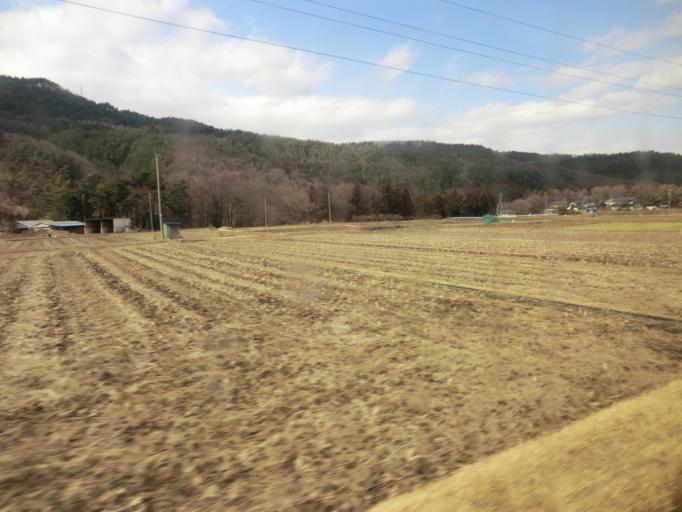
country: JP
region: Nagano
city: Shiojiri
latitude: 36.0756
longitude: 137.9065
